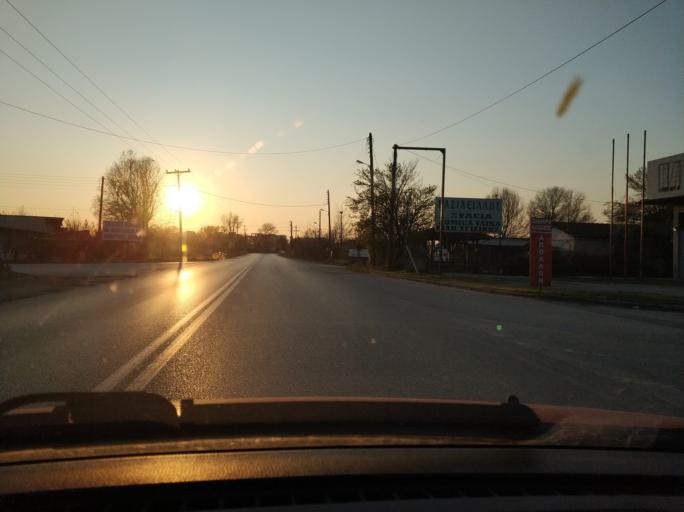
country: GR
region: Central Macedonia
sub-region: Nomos Thessalonikis
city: Lagkadas
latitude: 40.7458
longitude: 23.0809
